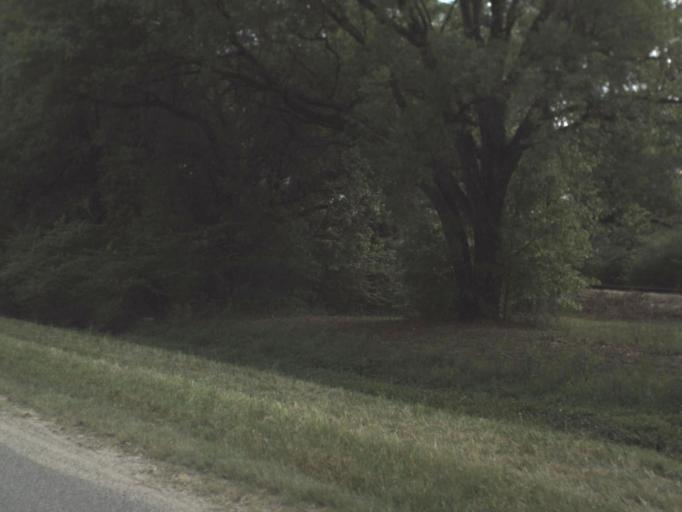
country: US
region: Florida
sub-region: Escambia County
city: Ensley
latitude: 30.5472
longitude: -87.2828
